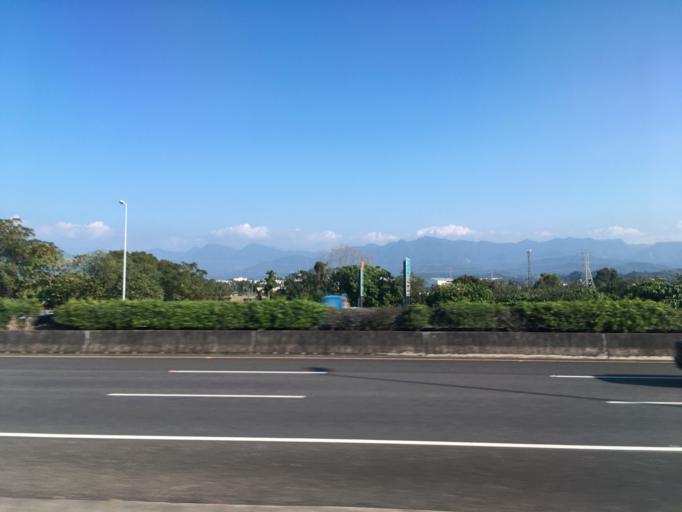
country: TW
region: Taiwan
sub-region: Chiayi
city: Jiayi Shi
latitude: 23.4476
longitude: 120.4832
